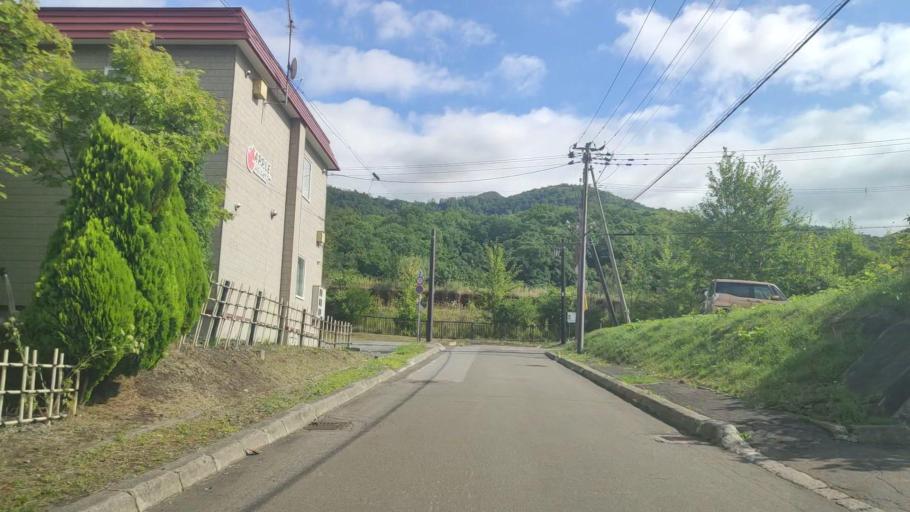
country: JP
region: Hokkaido
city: Date
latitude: 42.5620
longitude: 140.8256
